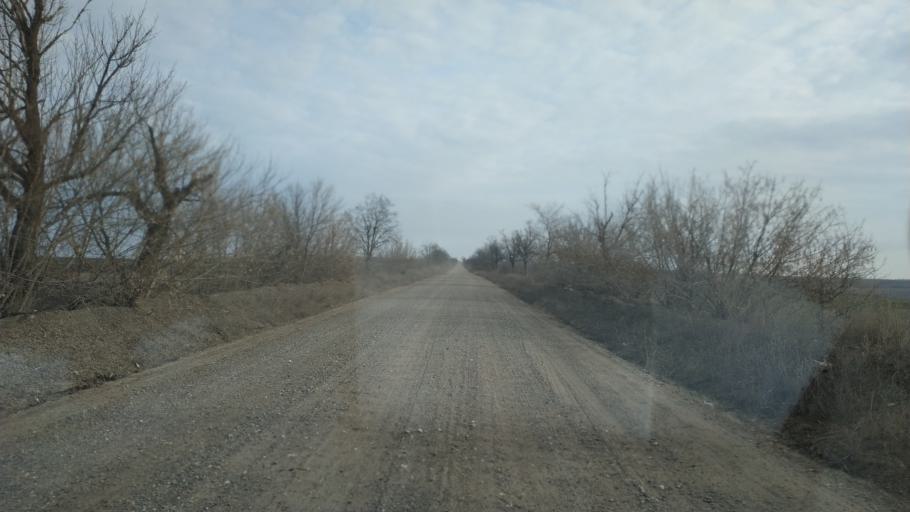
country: MD
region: Chisinau
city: Vadul lui Voda
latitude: 46.9796
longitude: 29.0810
